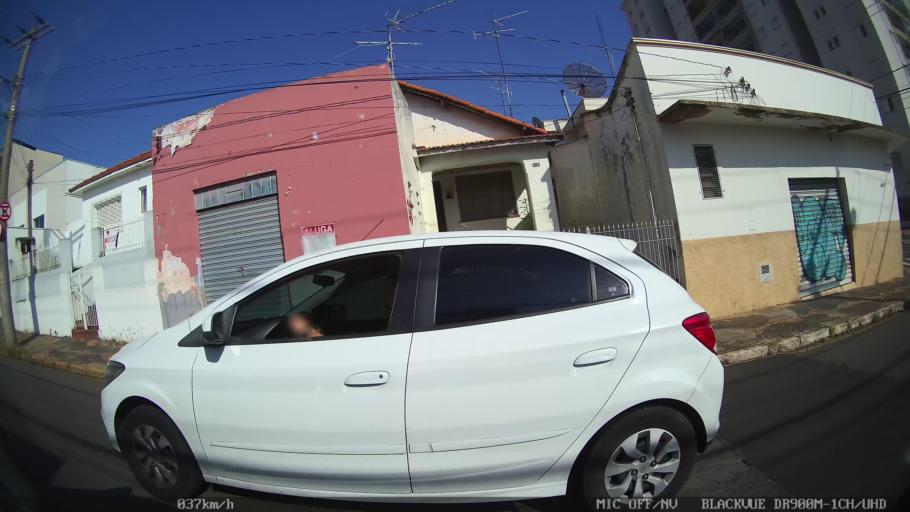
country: BR
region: Sao Paulo
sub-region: Americana
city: Americana
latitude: -22.7463
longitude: -47.3265
